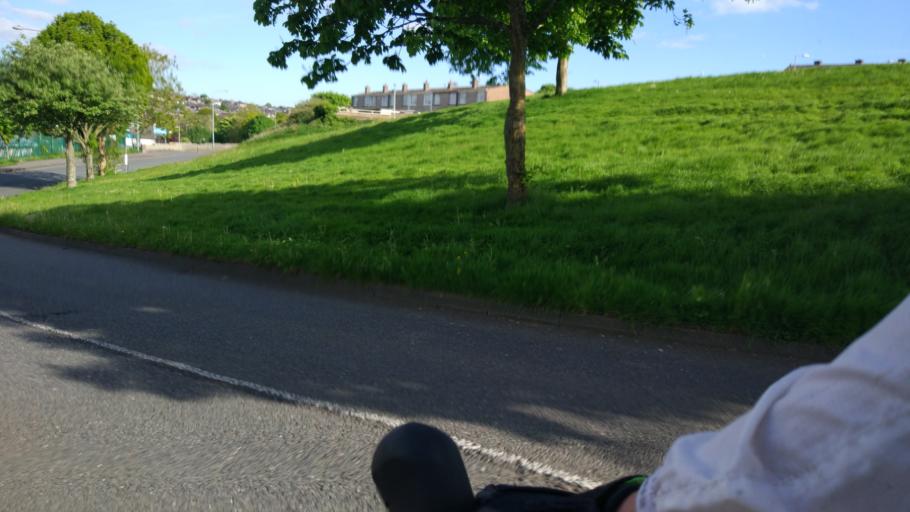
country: IE
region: Munster
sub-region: County Cork
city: Cork
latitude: 51.9115
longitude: -8.4598
